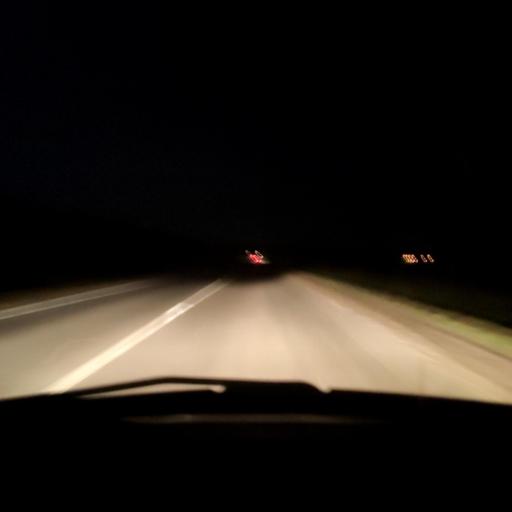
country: RU
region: Bashkortostan
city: Iglino
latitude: 54.8812
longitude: 56.4697
